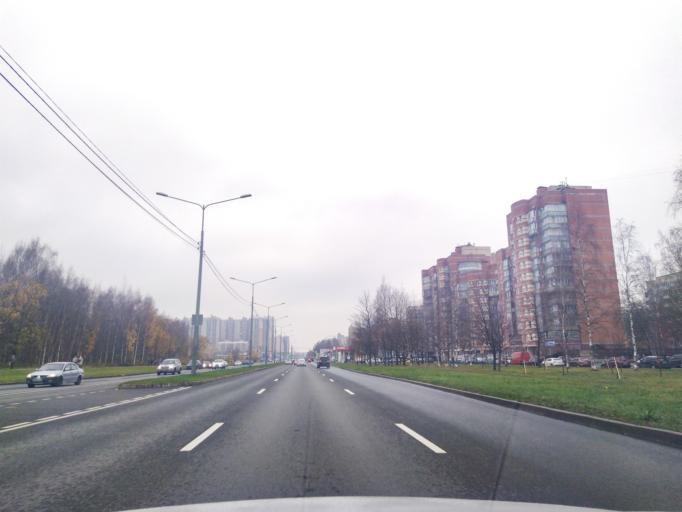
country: RU
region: St.-Petersburg
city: Sosnovka
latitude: 60.0316
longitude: 30.3496
